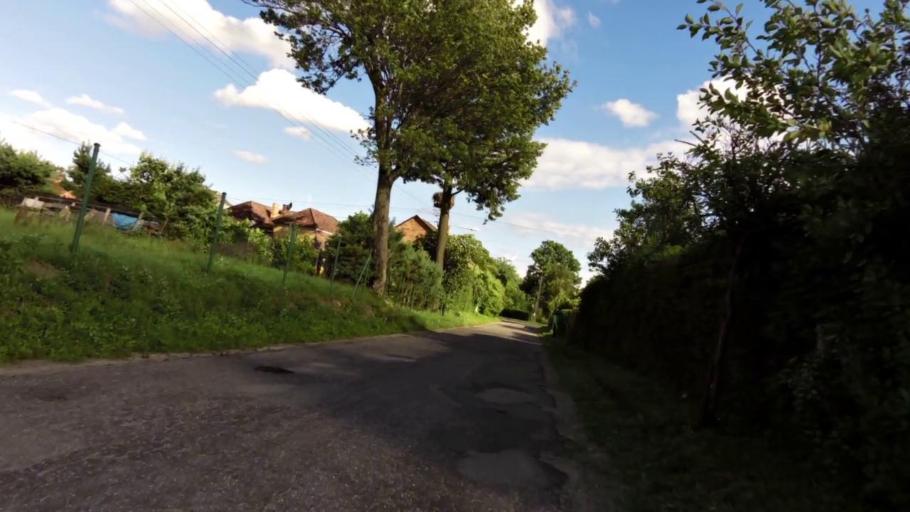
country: PL
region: West Pomeranian Voivodeship
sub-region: Powiat slawienski
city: Slawno
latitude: 54.4326
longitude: 16.7699
